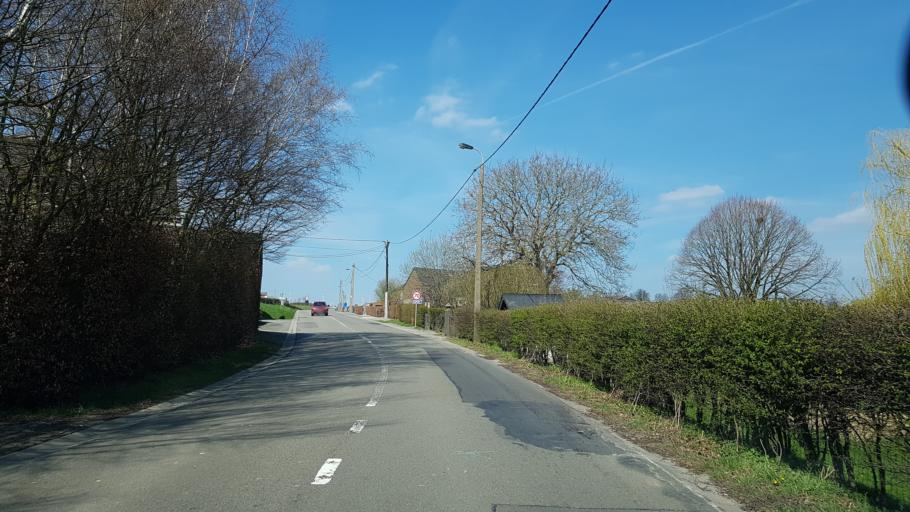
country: BE
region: Wallonia
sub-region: Province de Liege
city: Dison
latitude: 50.6485
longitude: 5.8880
